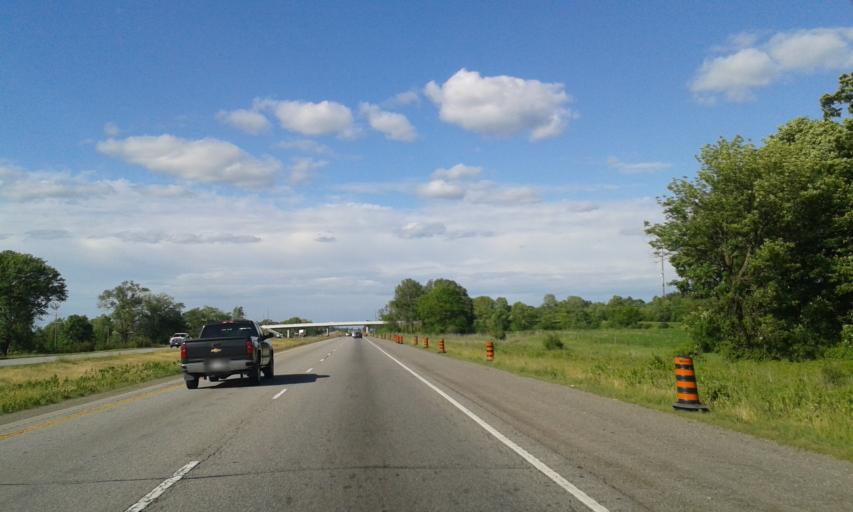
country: CA
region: Ontario
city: Prescott
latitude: 44.6933
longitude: -75.5777
